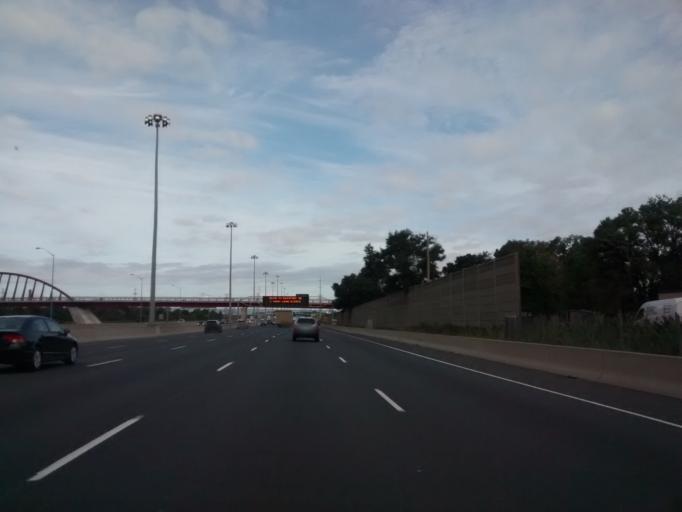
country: CA
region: Ontario
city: Hamilton
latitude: 43.2506
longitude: -79.7622
